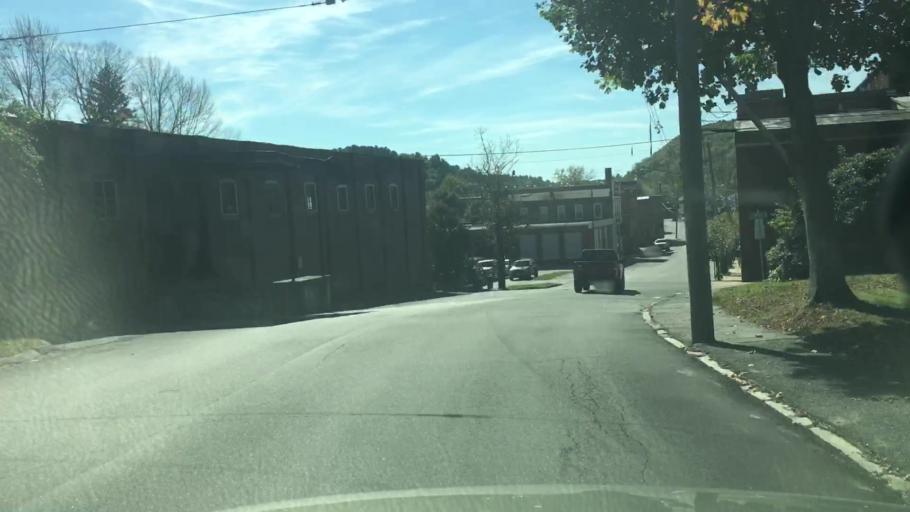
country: US
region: Connecticut
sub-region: Tolland County
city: Stafford Springs
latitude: 41.9556
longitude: -72.3022
